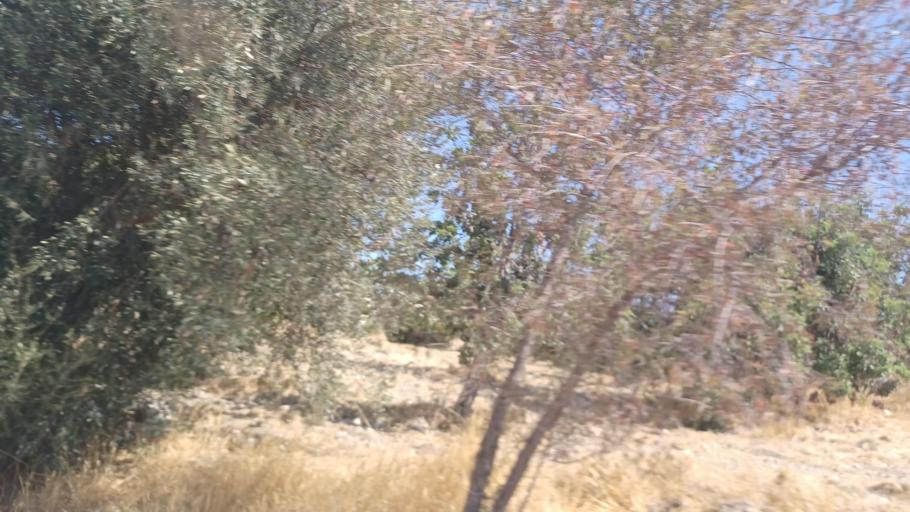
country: CY
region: Pafos
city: Polis
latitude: 35.0324
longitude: 32.5041
